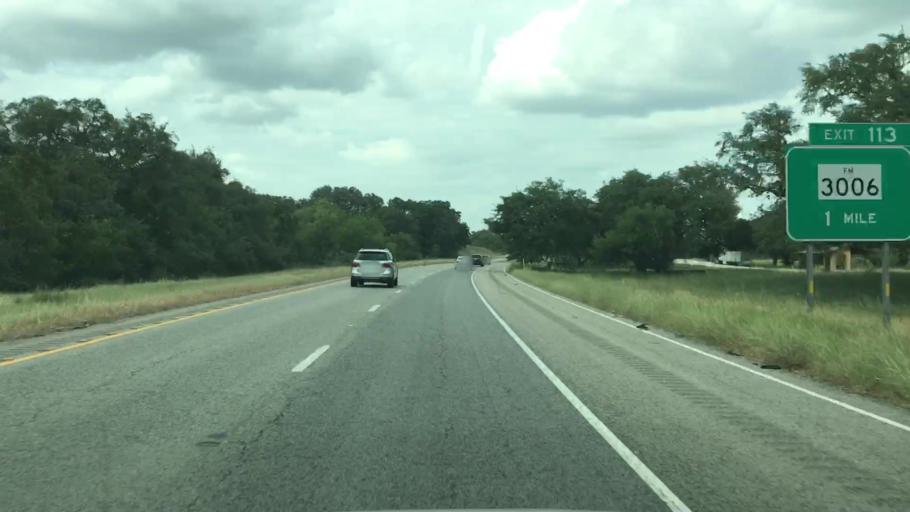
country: US
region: Texas
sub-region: Atascosa County
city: Pleasanton
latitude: 29.0333
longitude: -98.4324
